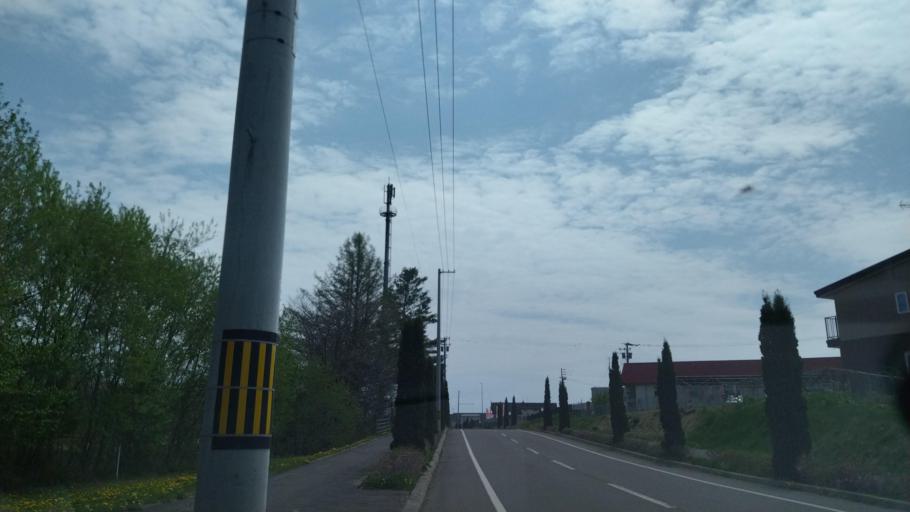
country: JP
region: Hokkaido
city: Otofuke
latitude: 43.2507
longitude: 143.5505
